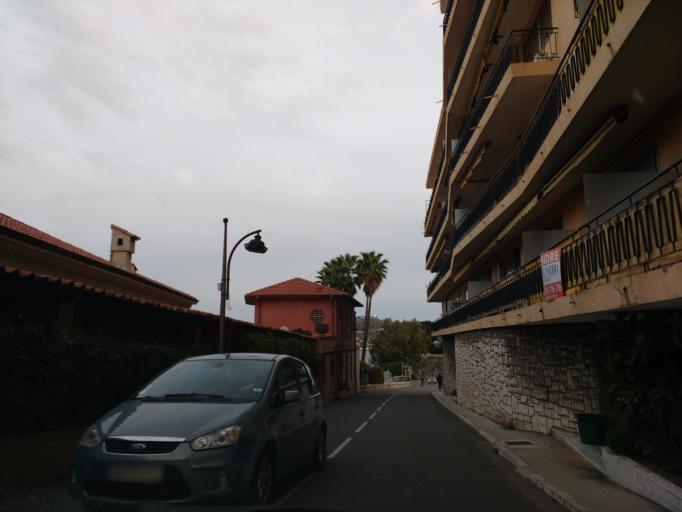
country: FR
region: Provence-Alpes-Cote d'Azur
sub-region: Departement des Alpes-Maritimes
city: Villefranche-sur-Mer
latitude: 43.7033
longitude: 7.3107
